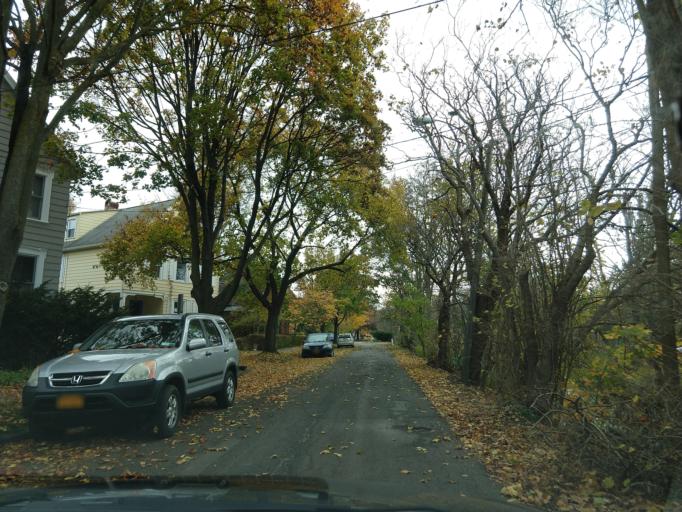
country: US
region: New York
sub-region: Tompkins County
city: Ithaca
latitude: 42.4467
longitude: -76.5007
